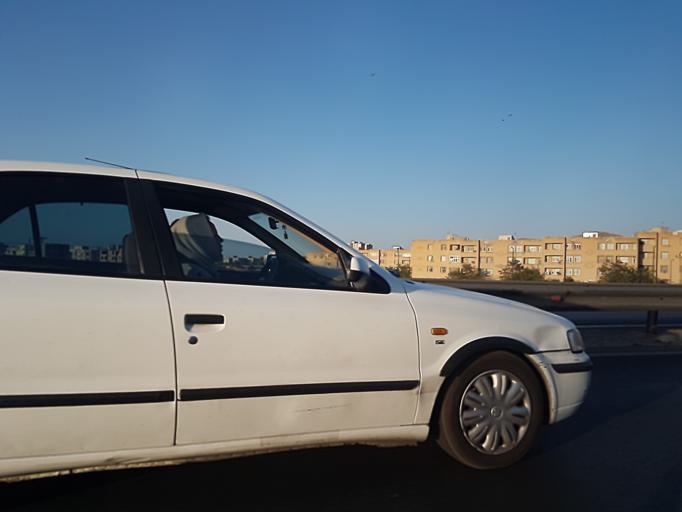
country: IR
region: Markazi
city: Arak
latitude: 34.0686
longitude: 49.7158
